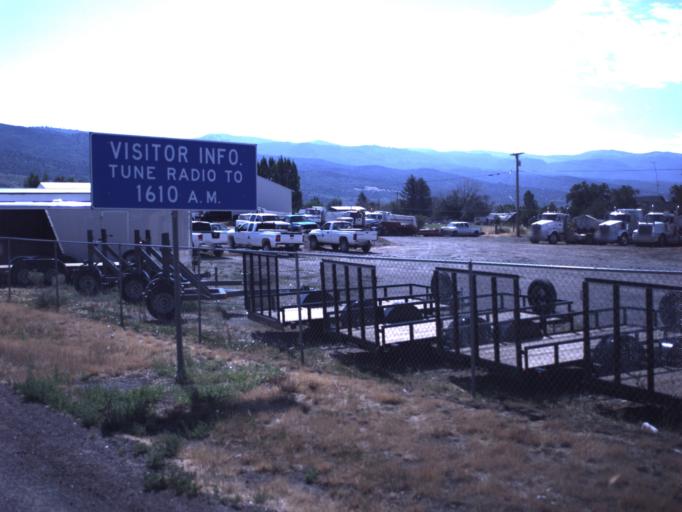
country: US
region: Utah
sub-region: Sanpete County
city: Fairview
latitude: 39.6344
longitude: -111.4360
